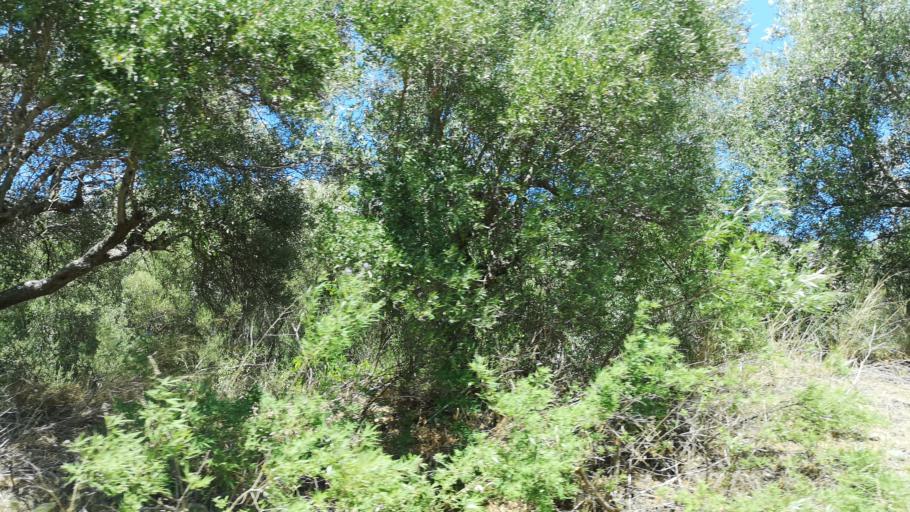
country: GR
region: Crete
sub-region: Nomos Lasithiou
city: Neapoli
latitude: 35.2430
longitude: 25.6437
